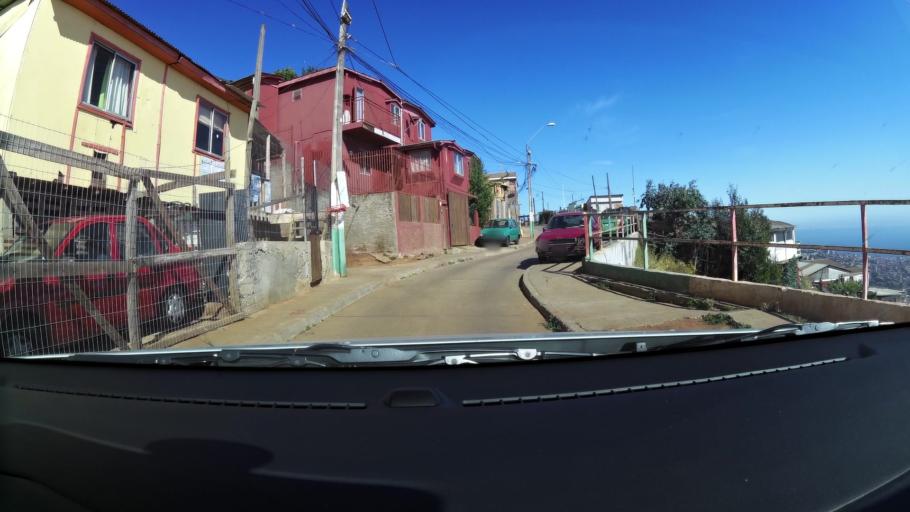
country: CL
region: Valparaiso
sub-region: Provincia de Valparaiso
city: Valparaiso
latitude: -33.0537
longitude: -71.6381
